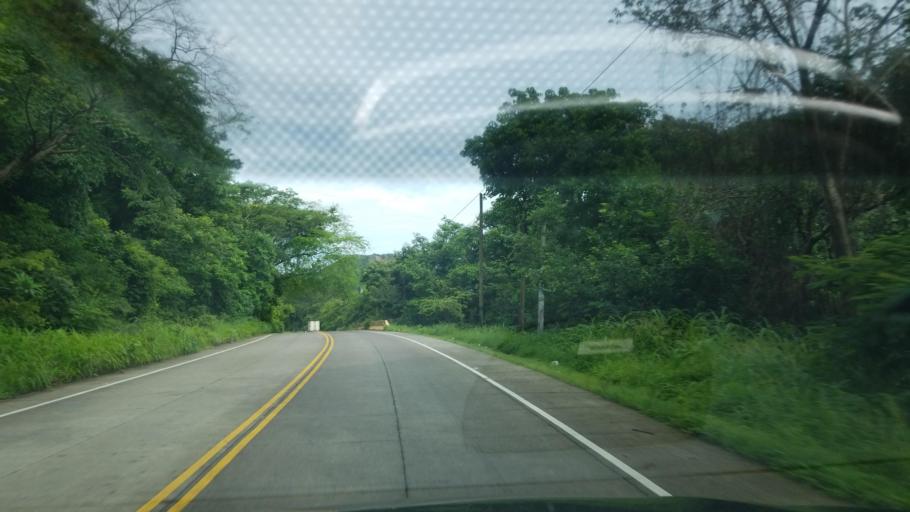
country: HN
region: Francisco Morazan
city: El Porvenir
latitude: 13.6858
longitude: -87.3481
